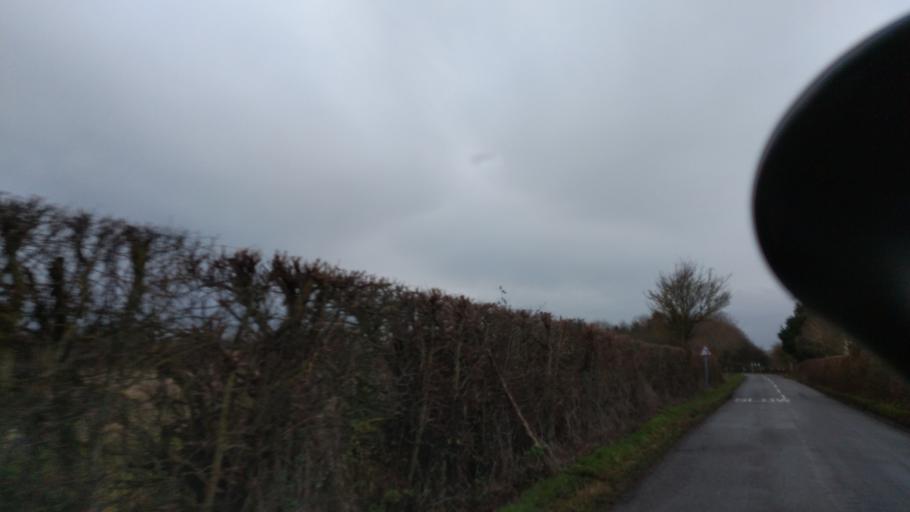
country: GB
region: England
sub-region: Borough of Swindon
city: Highworth
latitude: 51.6078
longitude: -1.7259
